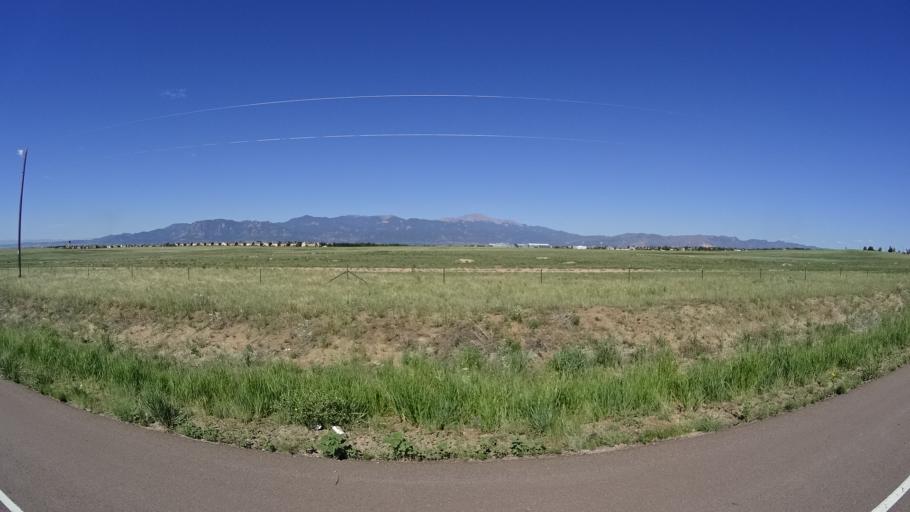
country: US
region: Colorado
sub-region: El Paso County
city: Cimarron Hills
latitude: 38.8337
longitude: -104.6828
